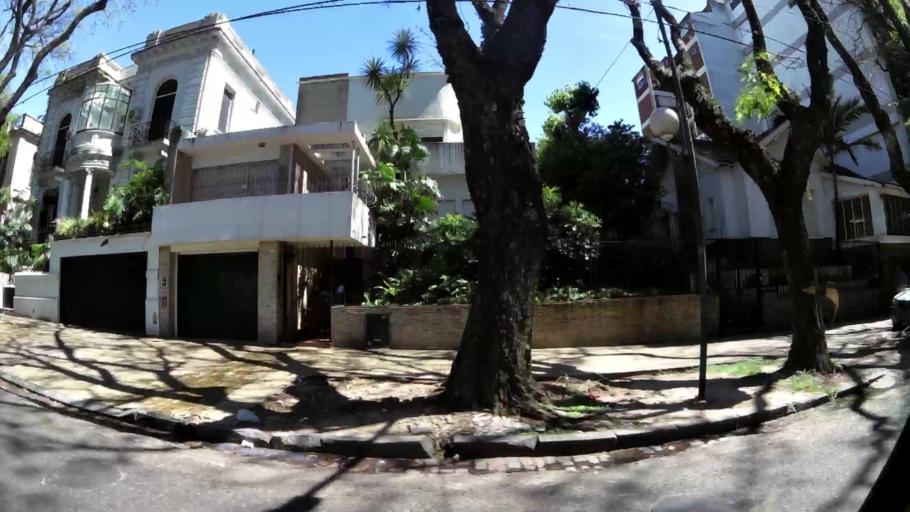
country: AR
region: Buenos Aires
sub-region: Partido de Vicente Lopez
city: Olivos
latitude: -34.5095
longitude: -58.4818
